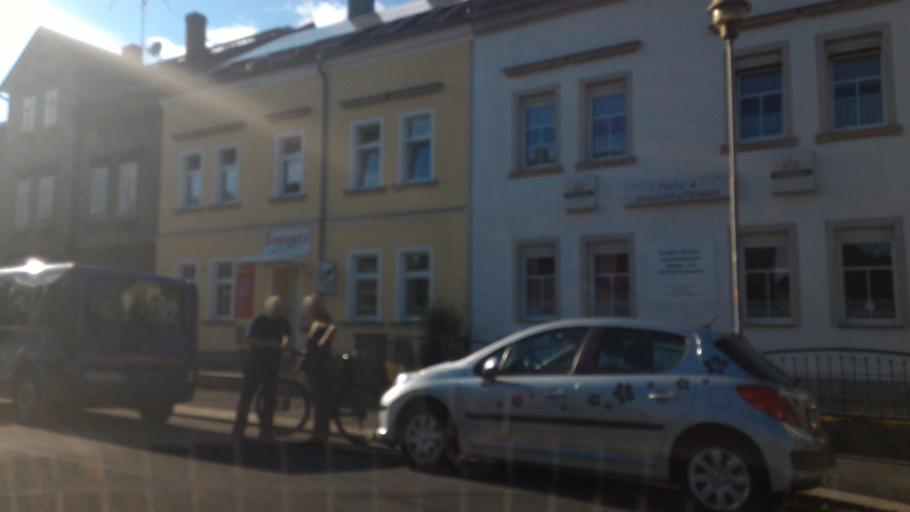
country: DE
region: Saxony
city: Zittau
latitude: 50.8977
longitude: 14.7898
